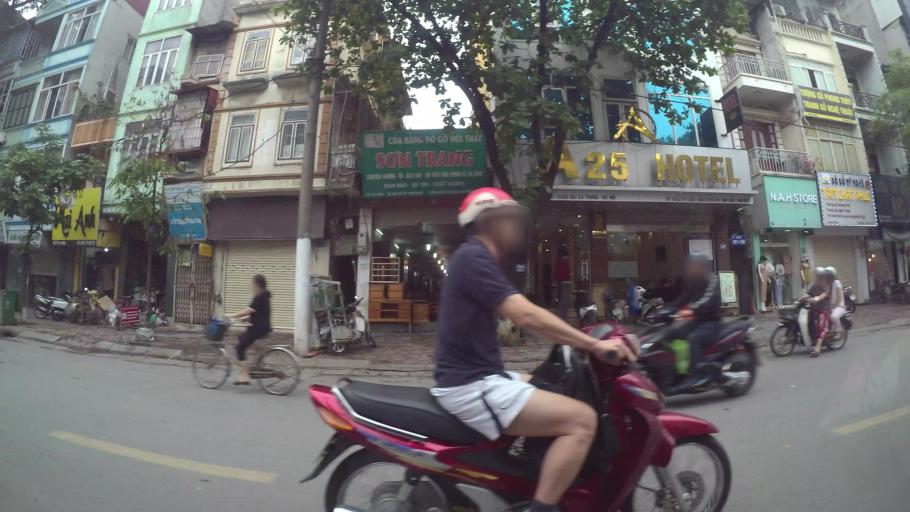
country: VN
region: Ha Noi
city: Hai BaTrung
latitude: 21.0098
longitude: 105.8606
